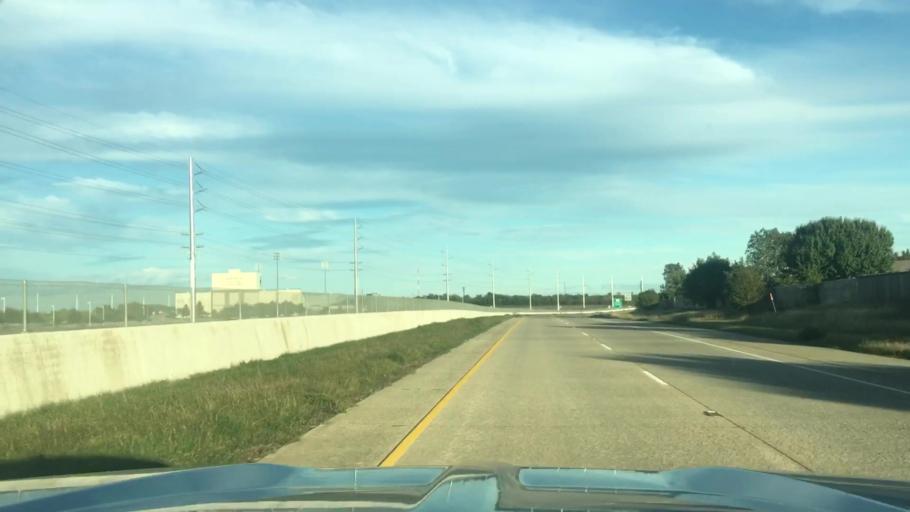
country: US
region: Texas
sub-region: Denton County
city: Denton
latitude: 33.2601
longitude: -97.1198
